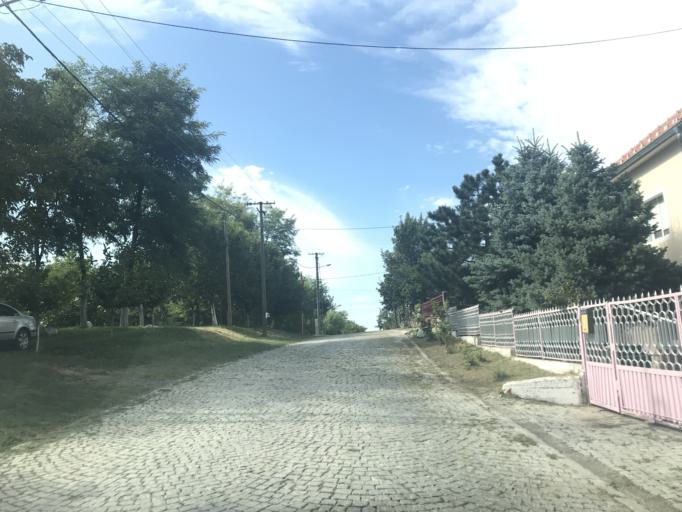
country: RS
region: Autonomna Pokrajina Vojvodina
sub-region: Juznobacki Okrug
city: Novi Sad
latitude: 45.2079
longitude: 19.8013
